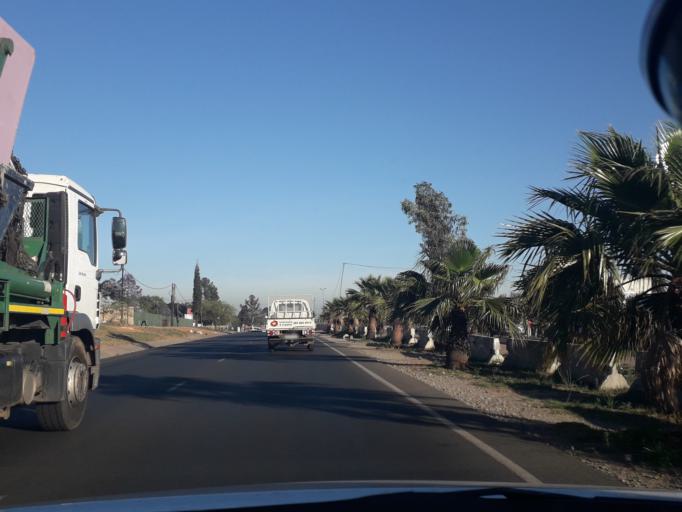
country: ZA
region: Gauteng
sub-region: West Rand District Municipality
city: Muldersdriseloop
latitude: -26.0657
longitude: 27.9068
